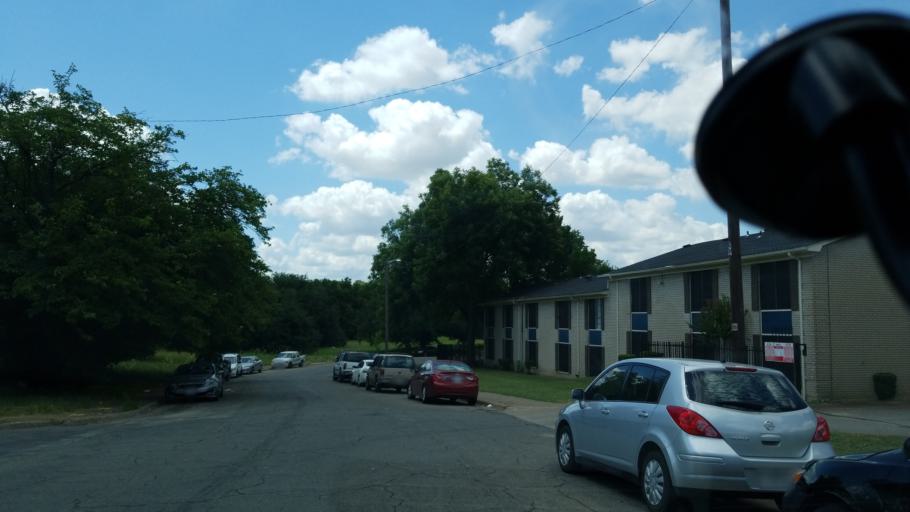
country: US
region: Texas
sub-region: Dallas County
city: Cockrell Hill
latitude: 32.6987
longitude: -96.8430
